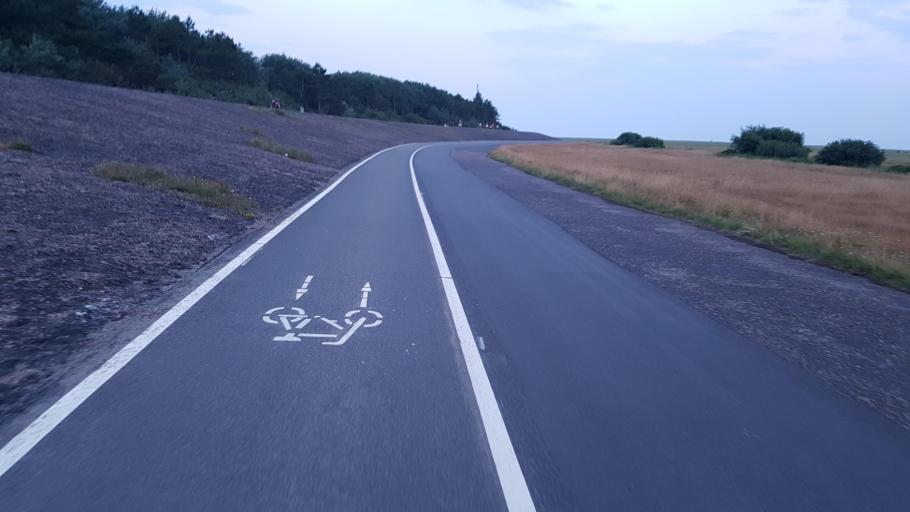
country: DE
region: Schleswig-Holstein
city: Sankt Peter-Ording
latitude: 54.2897
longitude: 8.6483
